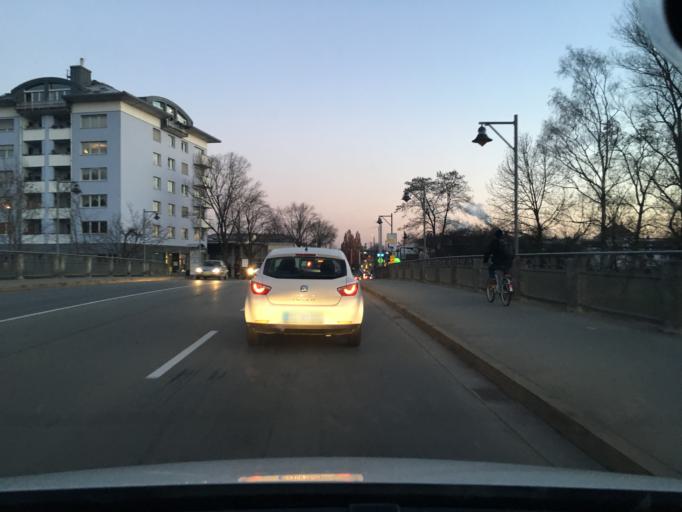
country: DE
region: Bavaria
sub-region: Upper Bavaria
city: Rosenheim
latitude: 47.8447
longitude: 12.1243
